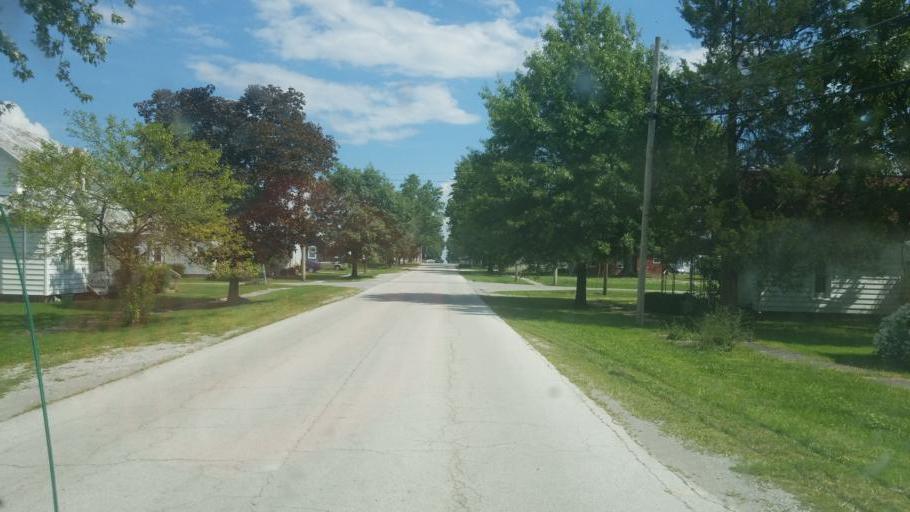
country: US
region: Ohio
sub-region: Hardin County
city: Forest
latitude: 40.8614
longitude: -83.4660
